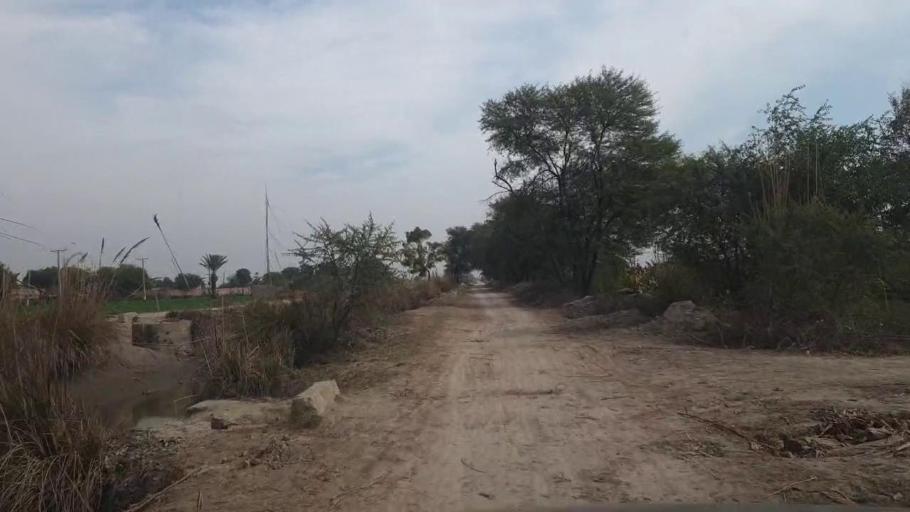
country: PK
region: Sindh
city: Nawabshah
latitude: 26.0770
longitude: 68.4505
